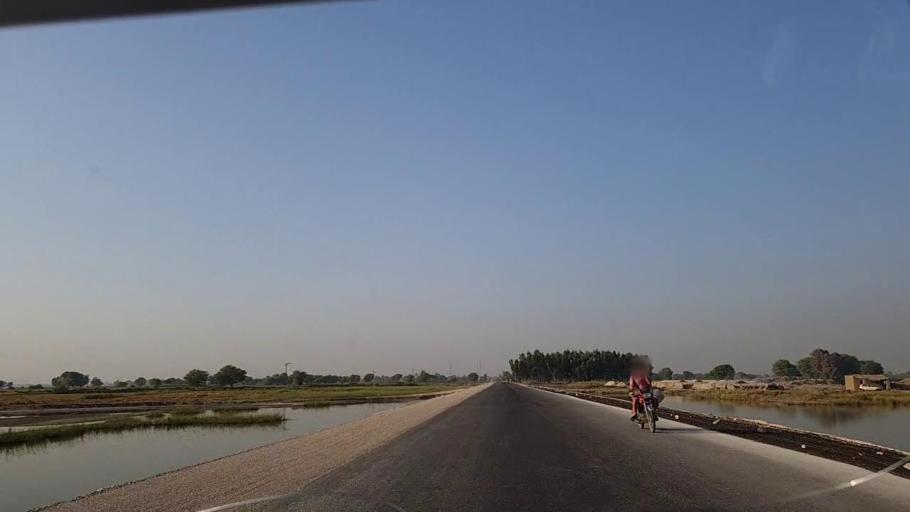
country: PK
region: Sindh
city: Rustam jo Goth
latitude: 27.9489
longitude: 68.8097
